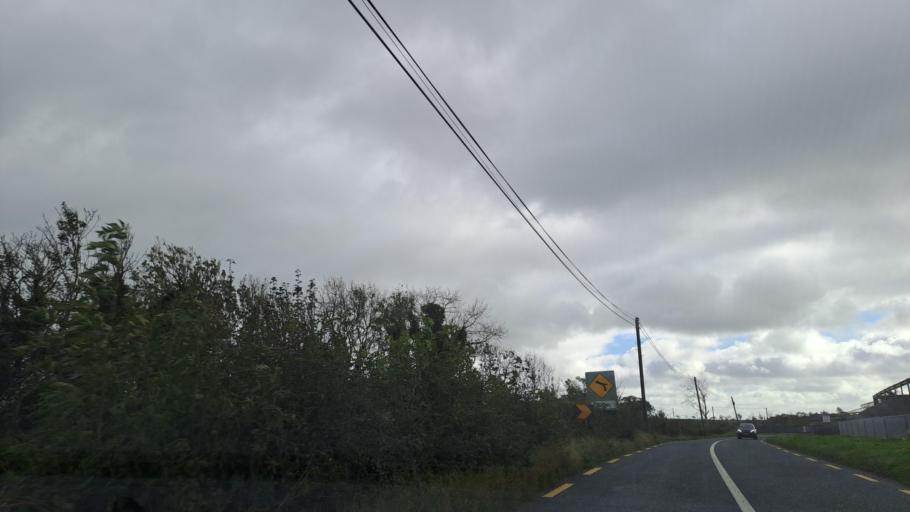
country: IE
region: Ulster
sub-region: An Cabhan
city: Kingscourt
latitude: 53.9127
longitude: -6.8473
